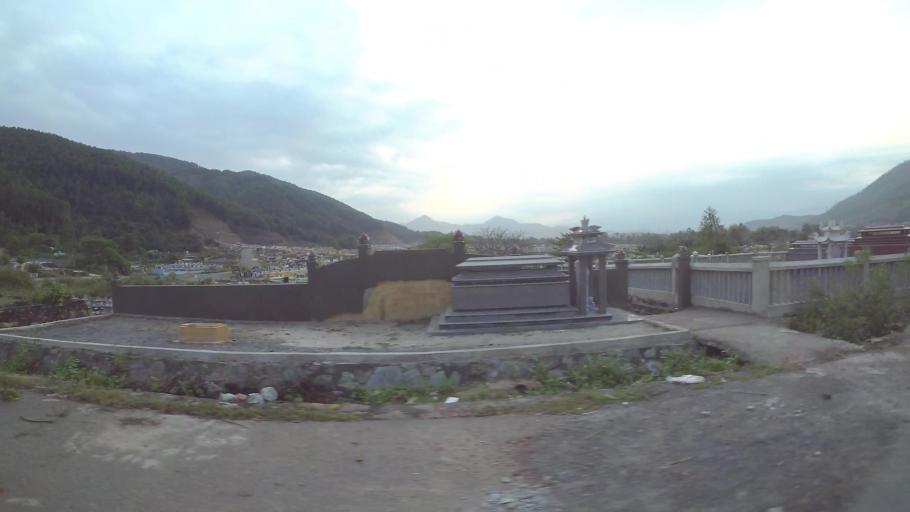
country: VN
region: Da Nang
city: Lien Chieu
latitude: 16.0572
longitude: 108.1270
